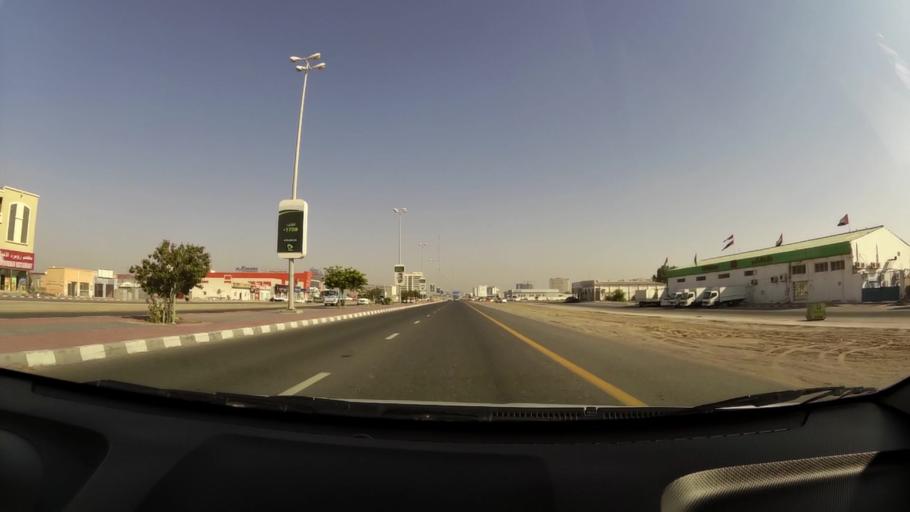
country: AE
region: Umm al Qaywayn
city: Umm al Qaywayn
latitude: 25.5044
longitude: 55.5488
